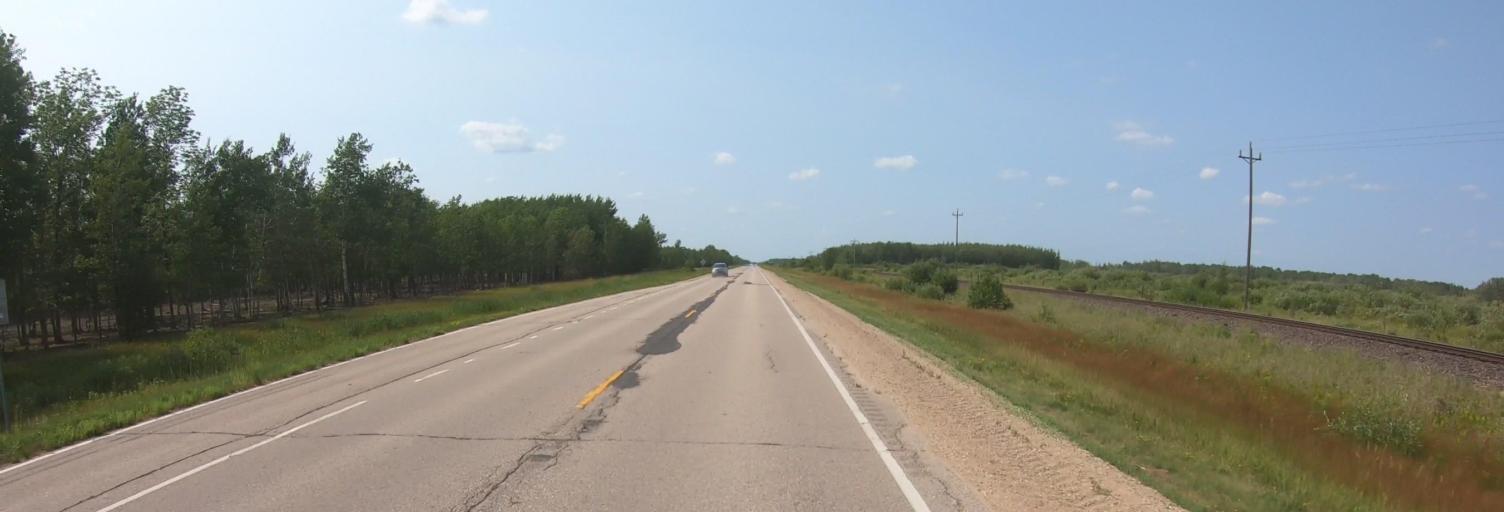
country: US
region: Minnesota
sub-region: Lake of the Woods County
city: Baudette
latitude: 48.7484
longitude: -94.8726
